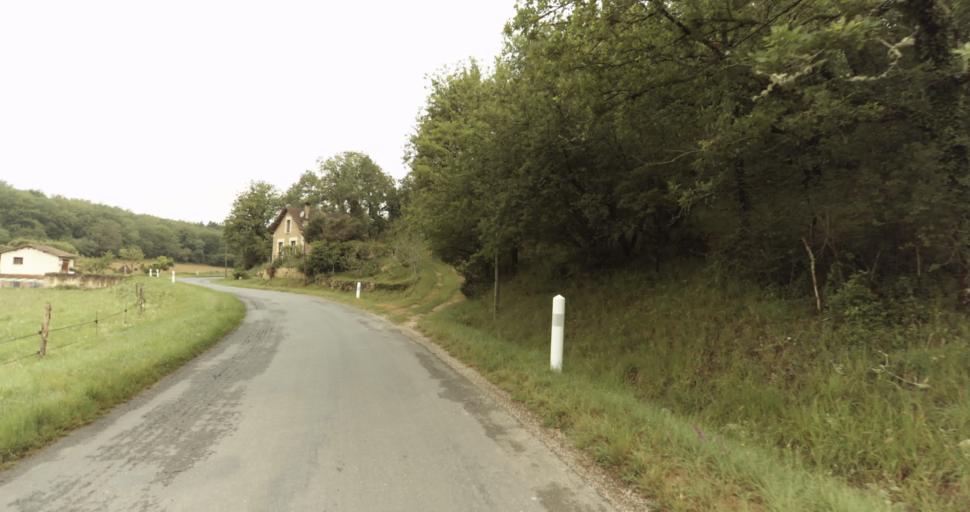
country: FR
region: Aquitaine
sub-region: Departement de la Dordogne
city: Lalinde
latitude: 44.8803
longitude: 0.7782
